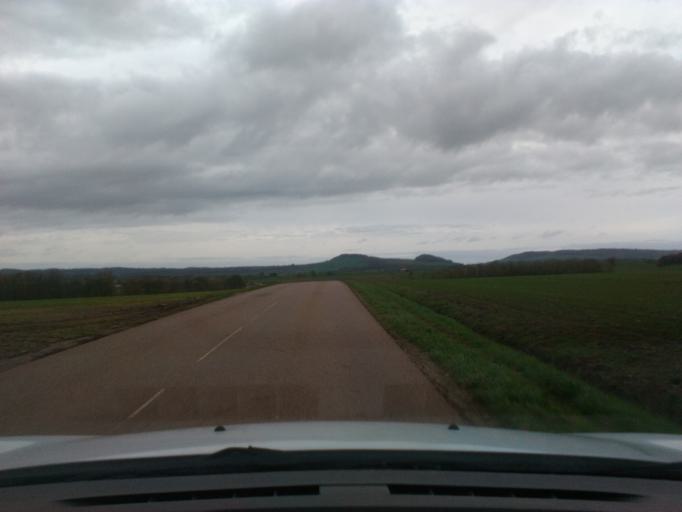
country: FR
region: Lorraine
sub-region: Departement des Vosges
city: Mirecourt
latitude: 48.3416
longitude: 6.1081
